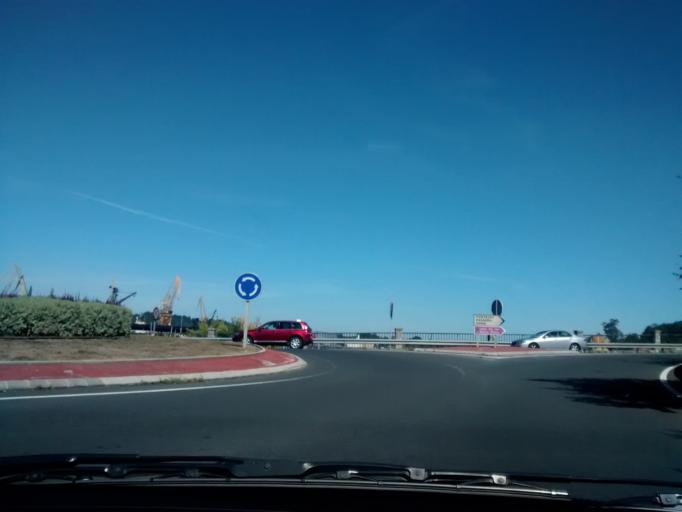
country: ES
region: Cantabria
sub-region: Provincia de Cantabria
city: El Astillero
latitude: 43.3986
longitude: -3.8144
